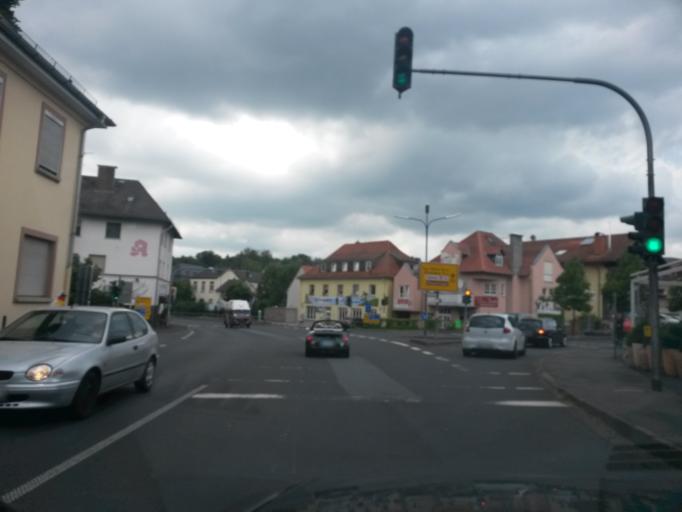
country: DE
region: Hesse
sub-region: Regierungsbezirk Kassel
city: Gersfeld
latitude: 50.4492
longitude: 9.9198
